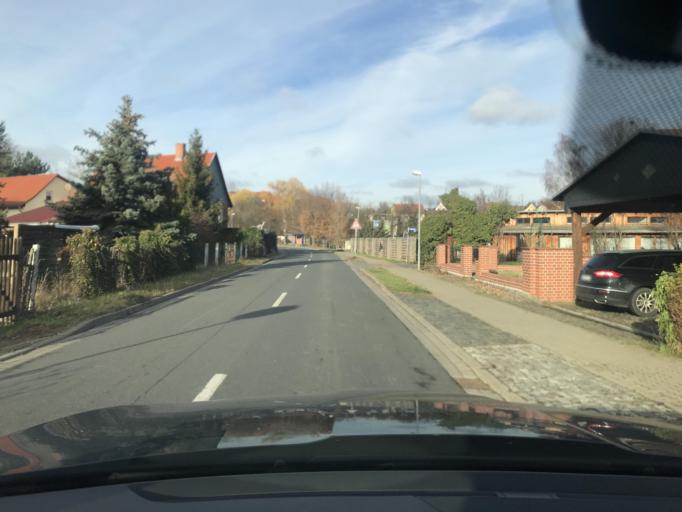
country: DE
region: Saxony-Anhalt
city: Weddersleben
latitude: 51.7628
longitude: 11.0885
